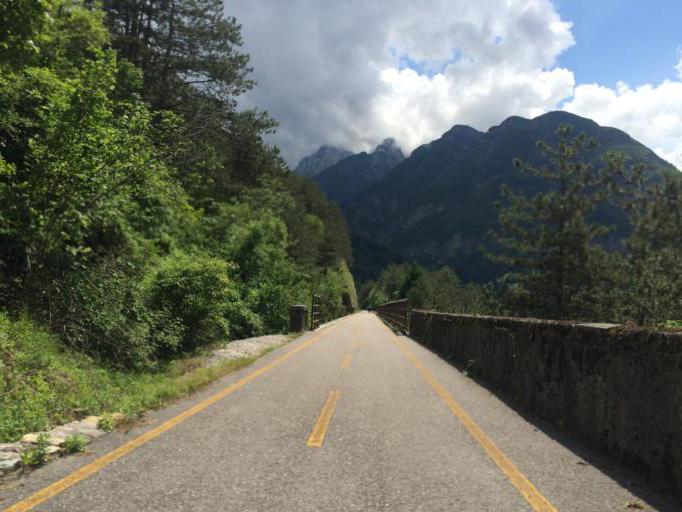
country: IT
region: Friuli Venezia Giulia
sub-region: Provincia di Udine
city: Dogna
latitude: 46.4584
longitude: 13.3058
